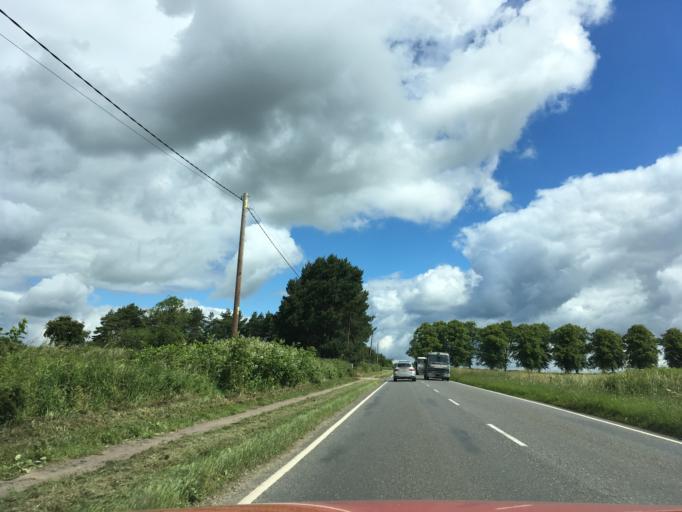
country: GB
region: England
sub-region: Oxfordshire
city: Chipping Norton
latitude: 51.9224
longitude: -1.5418
